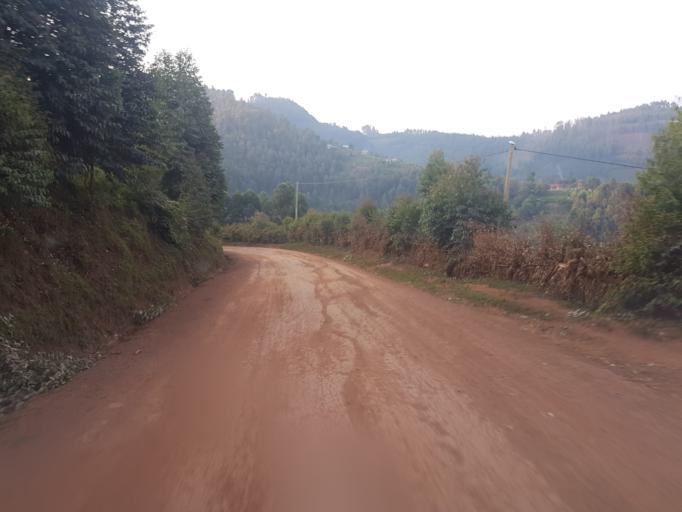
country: UG
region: Western Region
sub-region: Kanungu District
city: Kanungu
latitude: -0.9920
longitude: 29.8528
